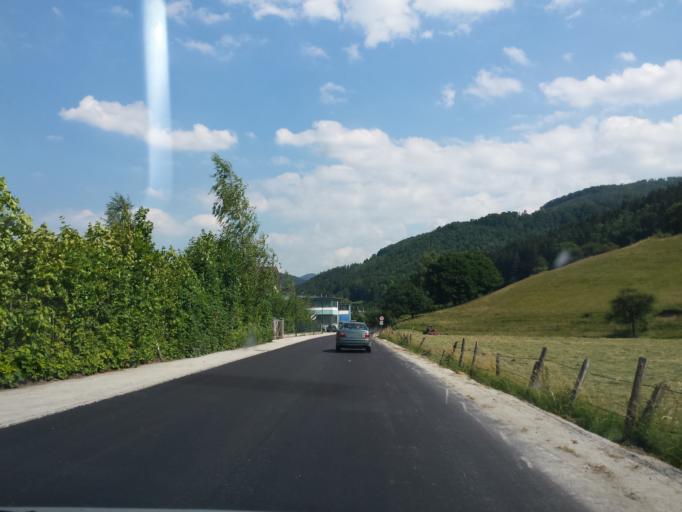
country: AT
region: Lower Austria
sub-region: Politischer Bezirk Lilienfeld
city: Ramsau
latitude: 48.0066
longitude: 15.7955
